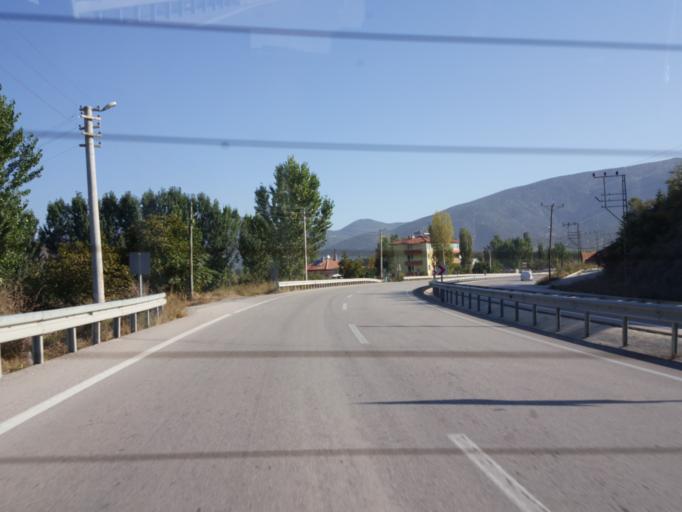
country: TR
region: Tokat
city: Turhal
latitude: 40.4125
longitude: 36.1029
